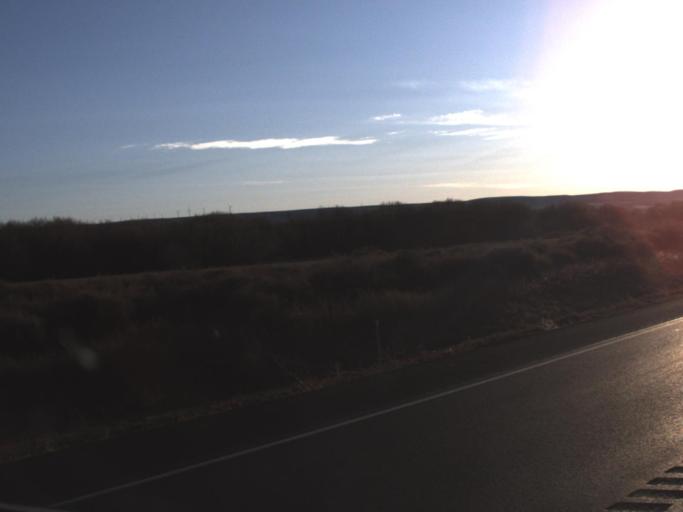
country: US
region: Washington
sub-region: Walla Walla County
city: Garrett
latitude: 46.0520
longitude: -118.6198
